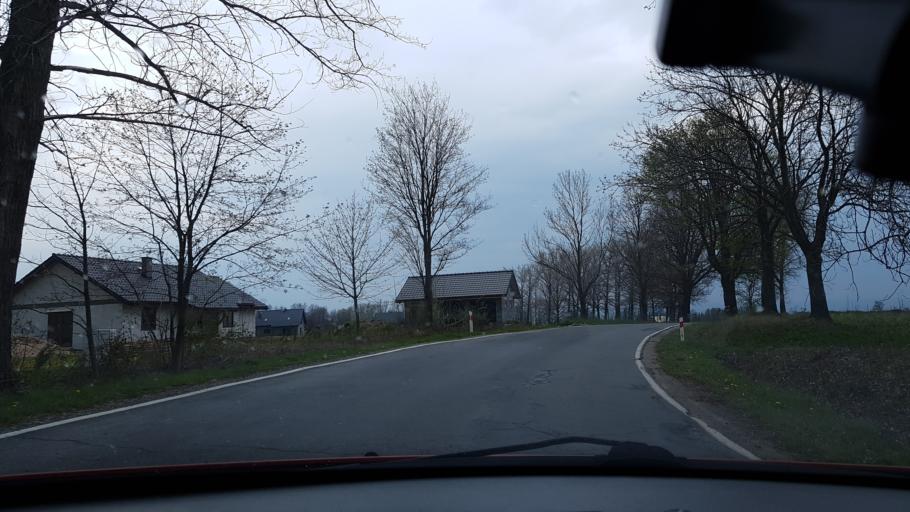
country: PL
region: Lower Silesian Voivodeship
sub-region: Powiat klodzki
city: Bystrzyca Klodzka
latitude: 50.3177
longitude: 16.6138
